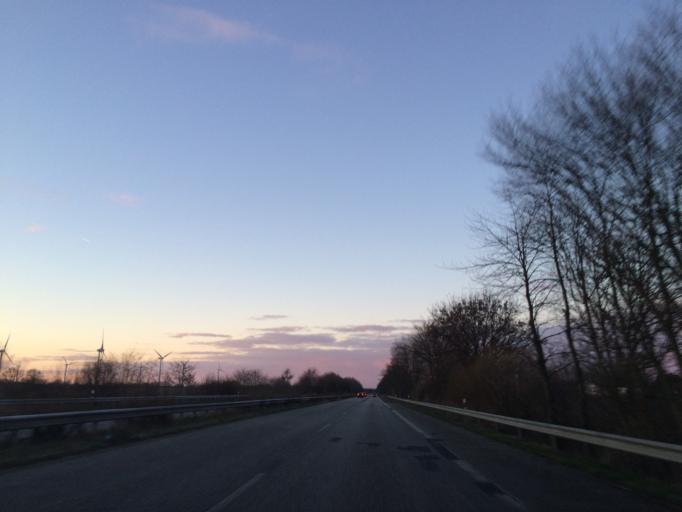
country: DE
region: Schleswig-Holstein
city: Beschendorf
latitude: 54.1688
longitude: 10.8780
